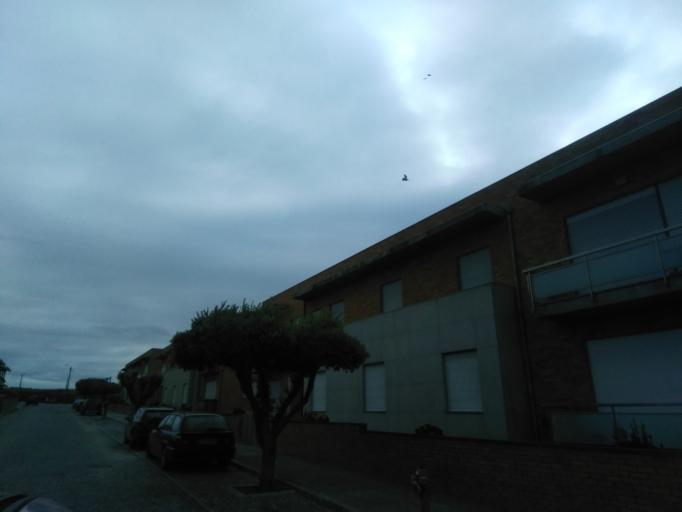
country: PT
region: Porto
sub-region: Matosinhos
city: Lavra
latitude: 41.2904
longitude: -8.7307
